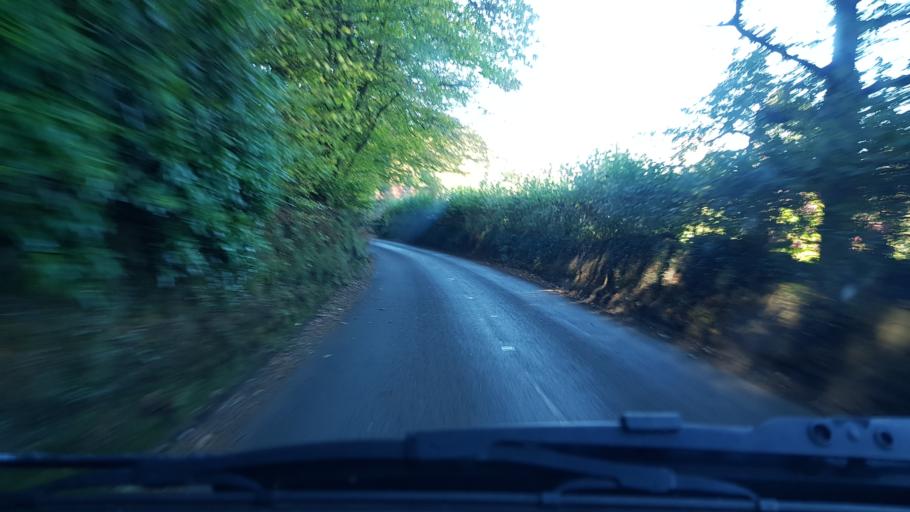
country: GB
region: England
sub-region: Surrey
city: Ockley
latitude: 51.1963
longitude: -0.4163
